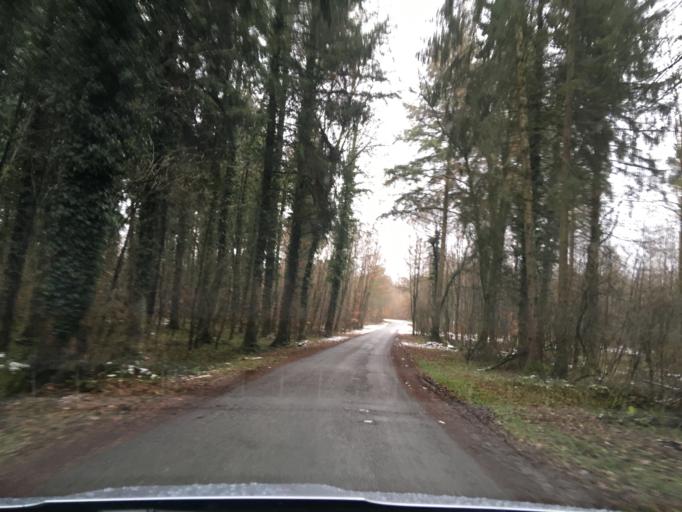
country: DE
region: Baden-Wuerttemberg
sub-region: Freiburg Region
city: Hilzingen
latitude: 47.7468
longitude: 8.8075
